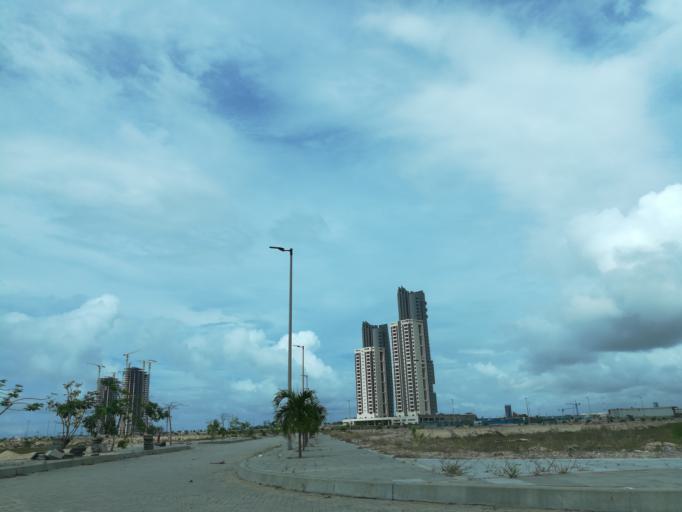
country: NG
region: Lagos
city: Ikoyi
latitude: 6.4101
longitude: 3.4152
